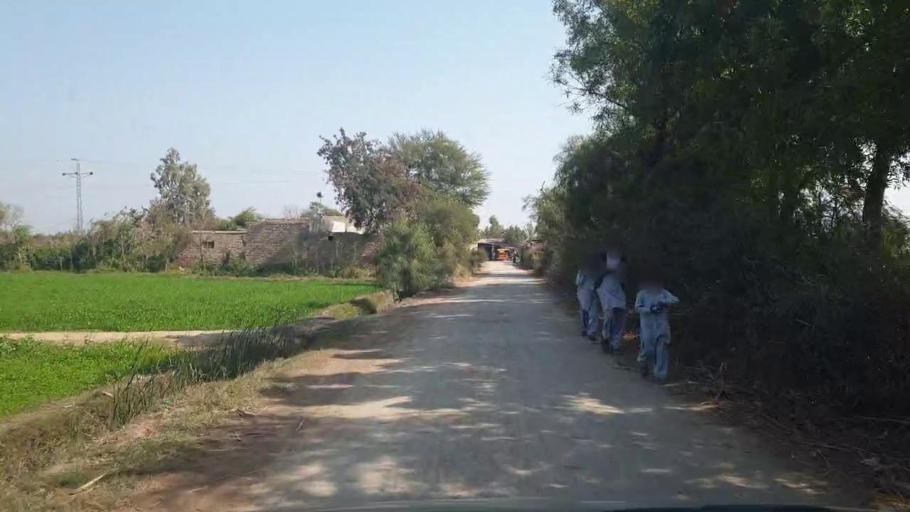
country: PK
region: Sindh
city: Tando Adam
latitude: 25.8202
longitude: 68.6548
